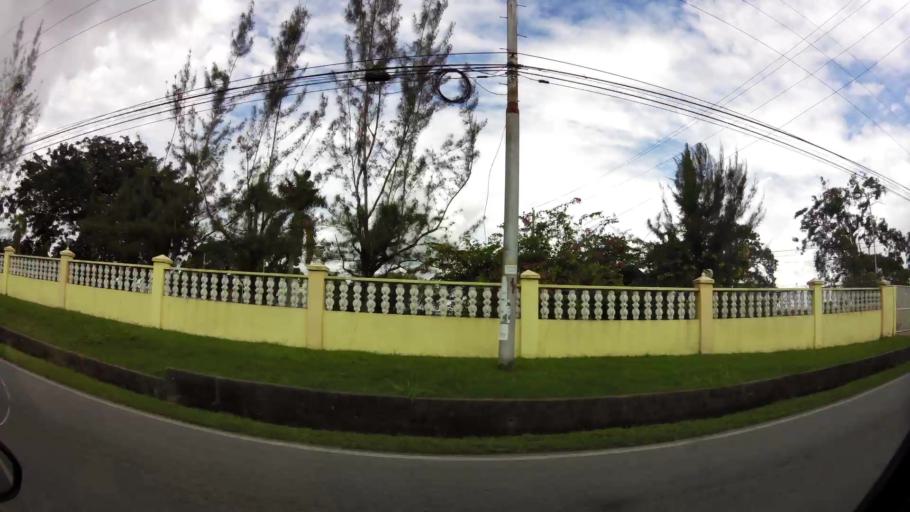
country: TT
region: Chaguanas
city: Chaguanas
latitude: 10.4670
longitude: -61.4168
